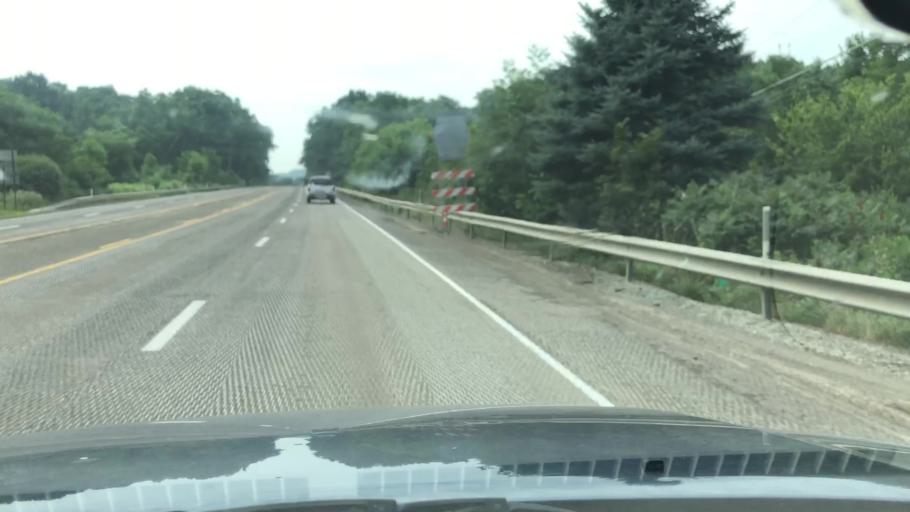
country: US
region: Pennsylvania
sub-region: Butler County
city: Nixon
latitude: 40.7413
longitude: -79.9251
